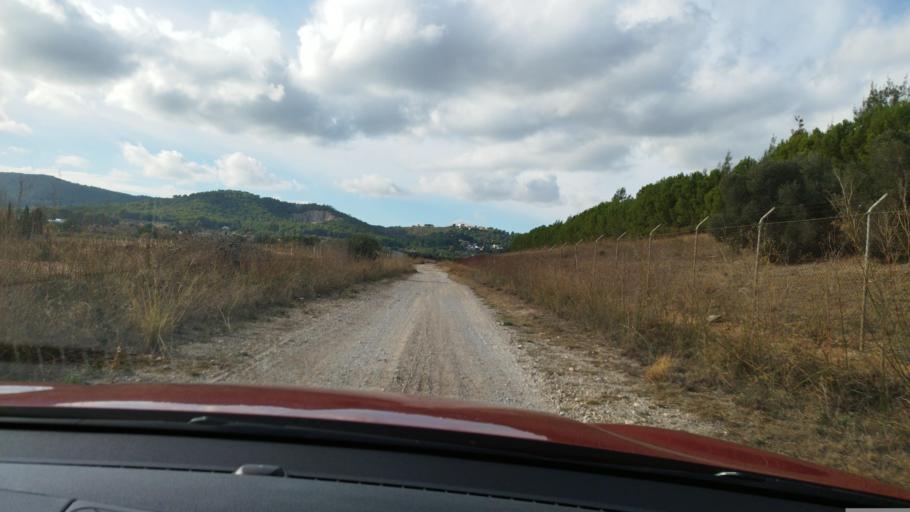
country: ES
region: Catalonia
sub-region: Provincia de Tarragona
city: Albinyana
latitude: 41.2595
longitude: 1.5083
